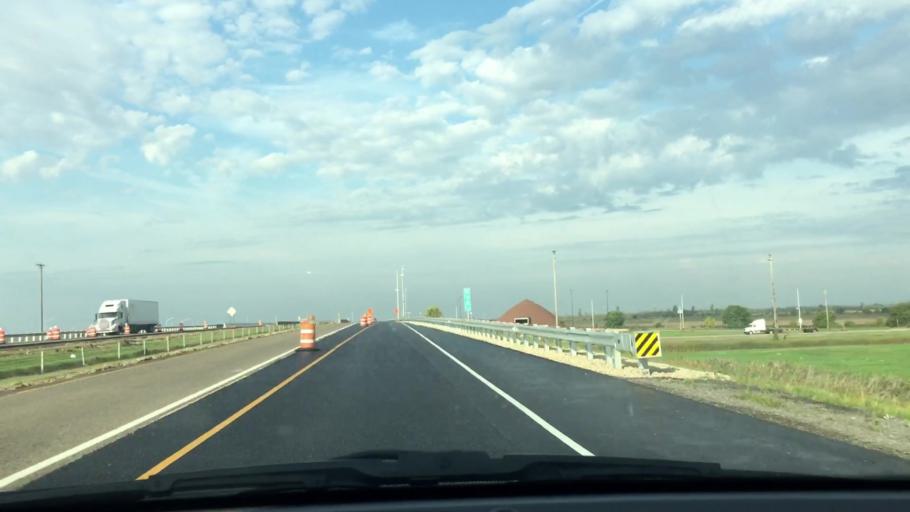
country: US
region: Illinois
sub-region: Ogle County
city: Rochelle
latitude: 41.9006
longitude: -89.0657
